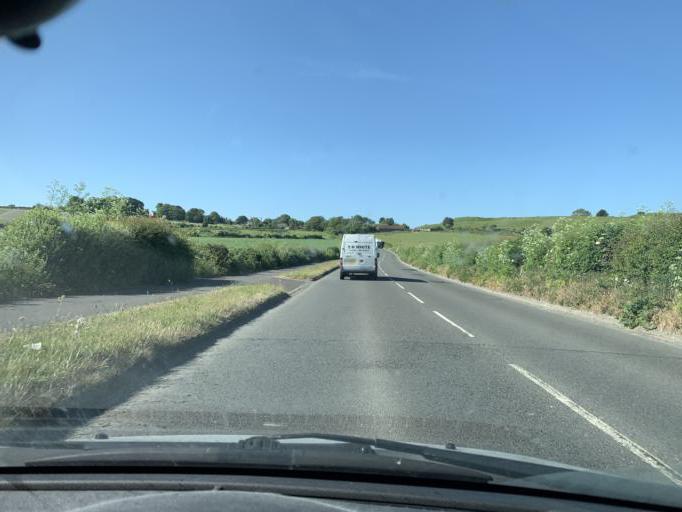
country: GB
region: England
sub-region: Wiltshire
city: Salisbury
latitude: 51.0969
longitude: -1.7976
